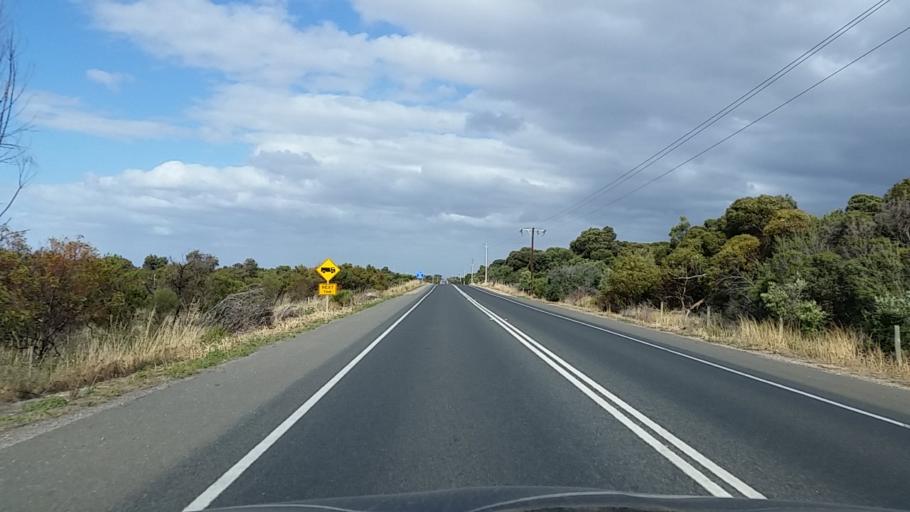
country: AU
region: South Australia
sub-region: Alexandrina
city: Goolwa
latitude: -35.5072
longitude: 138.7488
